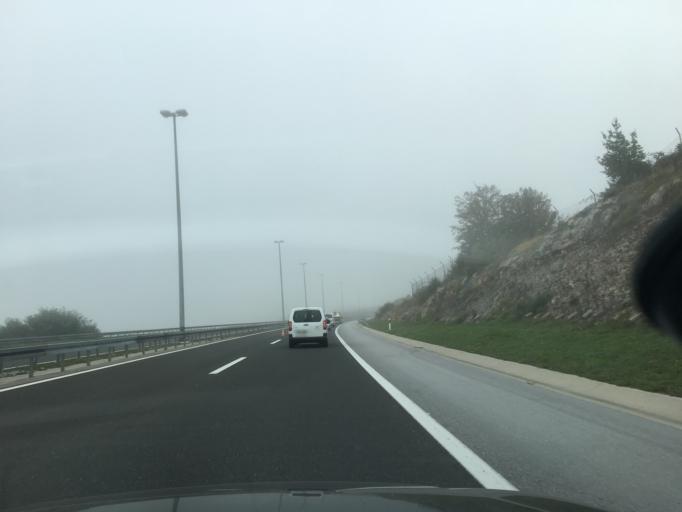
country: HR
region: Licko-Senjska
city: Brinje
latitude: 44.9592
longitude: 15.1039
